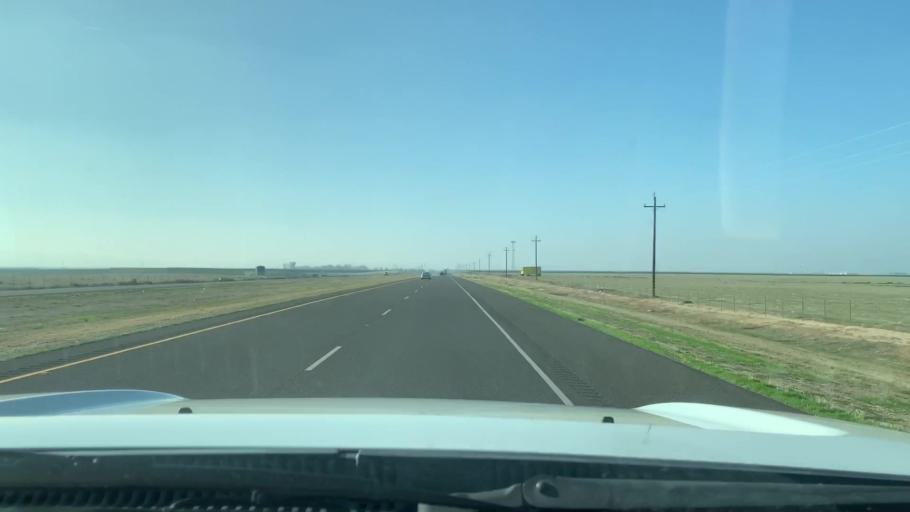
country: US
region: California
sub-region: Kern County
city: Lost Hills
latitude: 35.6155
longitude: -119.8375
